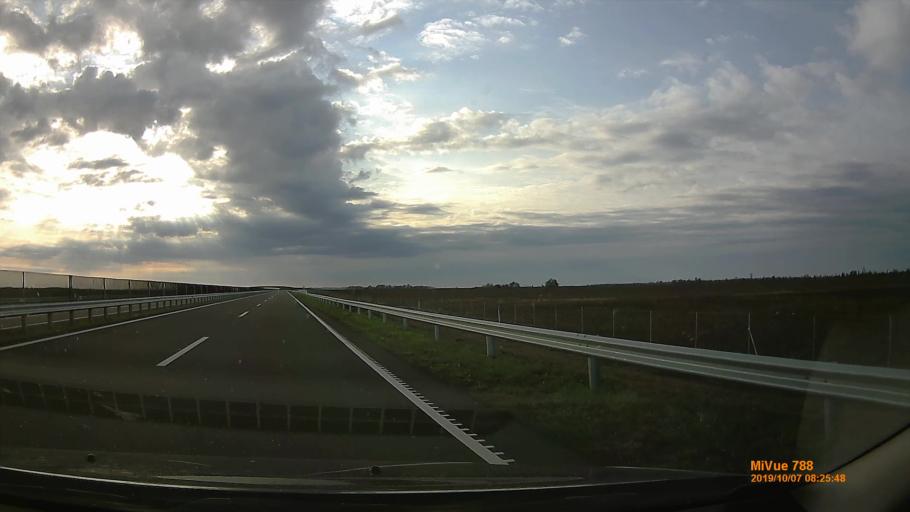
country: HU
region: Jasz-Nagykun-Szolnok
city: Kunszentmarton
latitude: 46.8262
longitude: 20.3616
